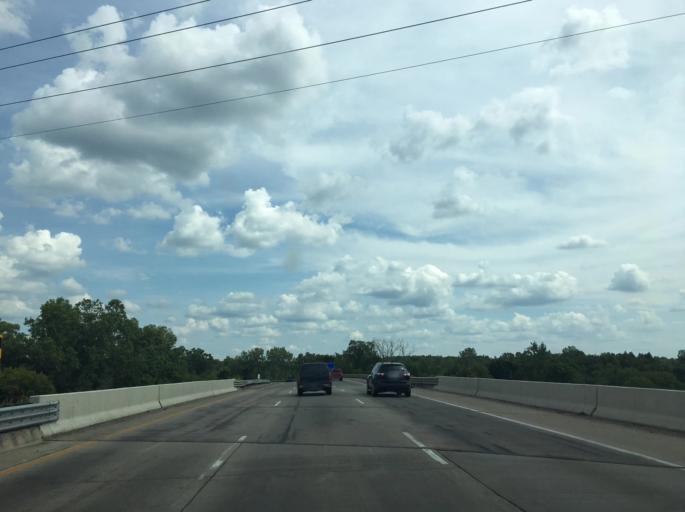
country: US
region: Michigan
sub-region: Genesee County
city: Grand Blanc
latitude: 42.9030
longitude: -83.6487
